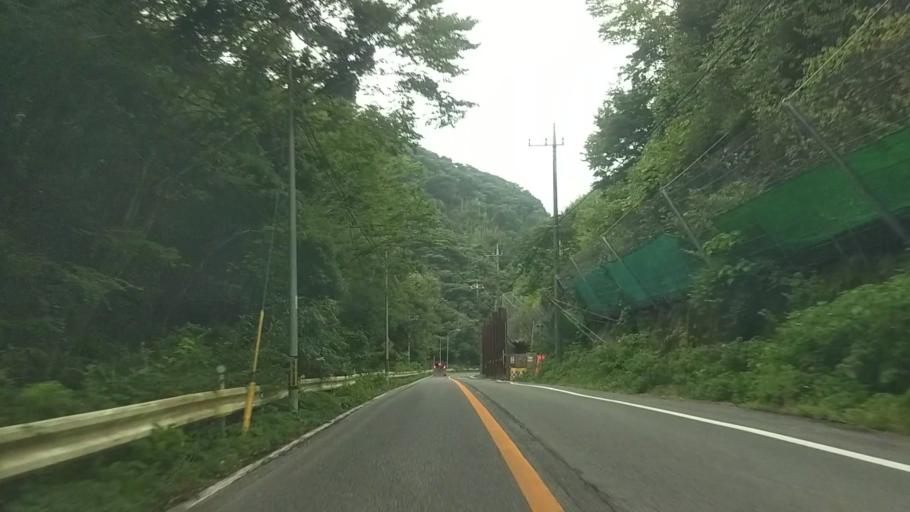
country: JP
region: Chiba
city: Tateyama
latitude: 35.1405
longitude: 139.9081
